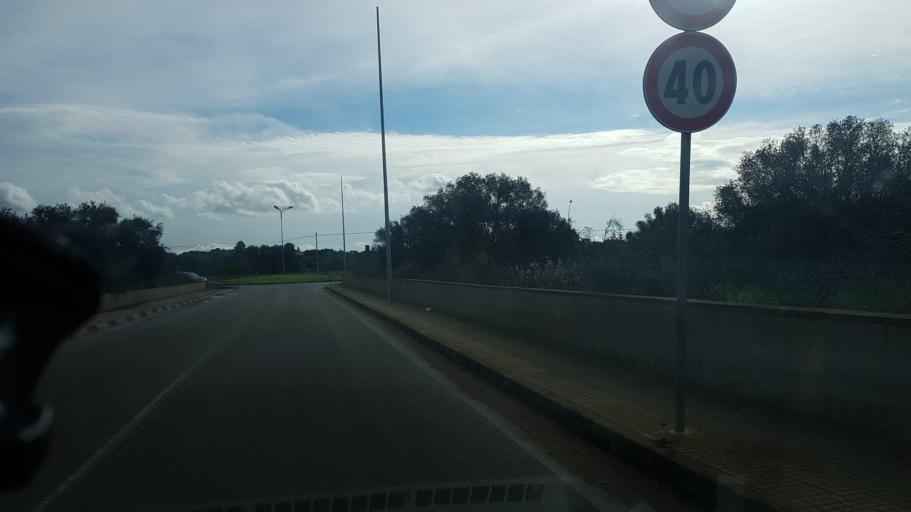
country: IT
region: Apulia
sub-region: Provincia di Brindisi
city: San Vito dei Normanni
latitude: 40.6617
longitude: 17.7156
